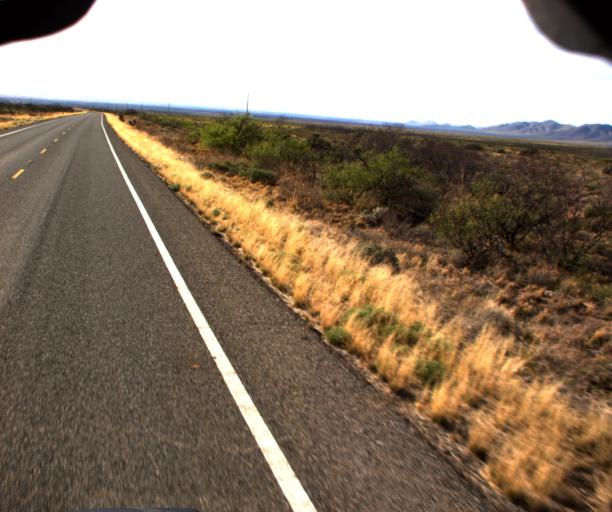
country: US
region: Arizona
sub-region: Cochise County
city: Willcox
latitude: 32.1851
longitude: -109.6735
